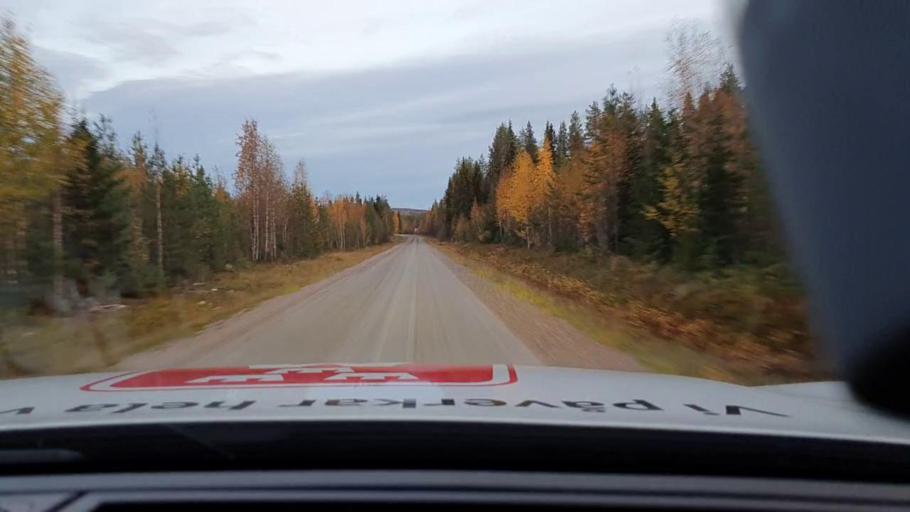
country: SE
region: Norrbotten
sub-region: Overkalix Kommun
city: OEverkalix
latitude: 66.2492
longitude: 23.2073
